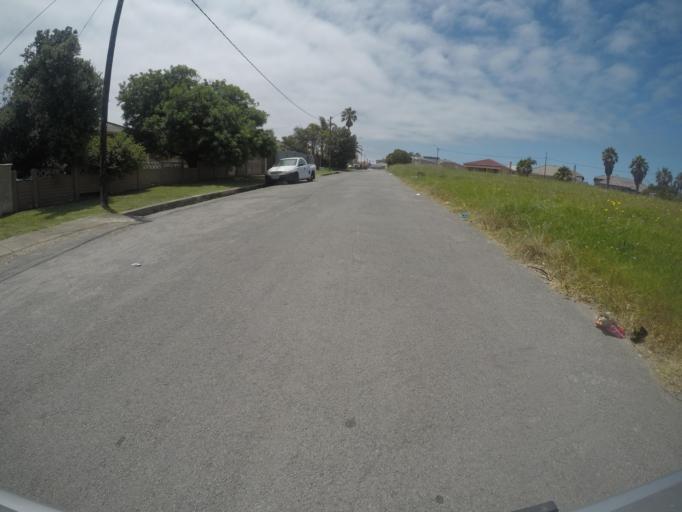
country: ZA
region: Eastern Cape
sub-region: Buffalo City Metropolitan Municipality
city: East London
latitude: -33.0211
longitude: 27.9098
